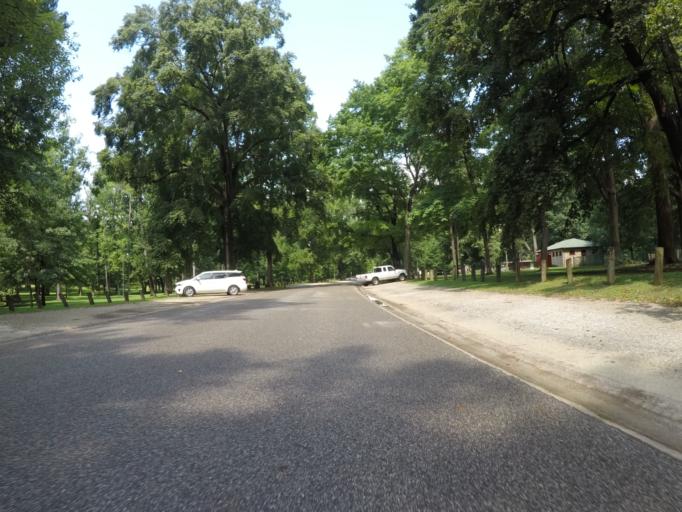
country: US
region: Kentucky
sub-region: Boyd County
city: Ashland
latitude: 38.4725
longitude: -82.6376
